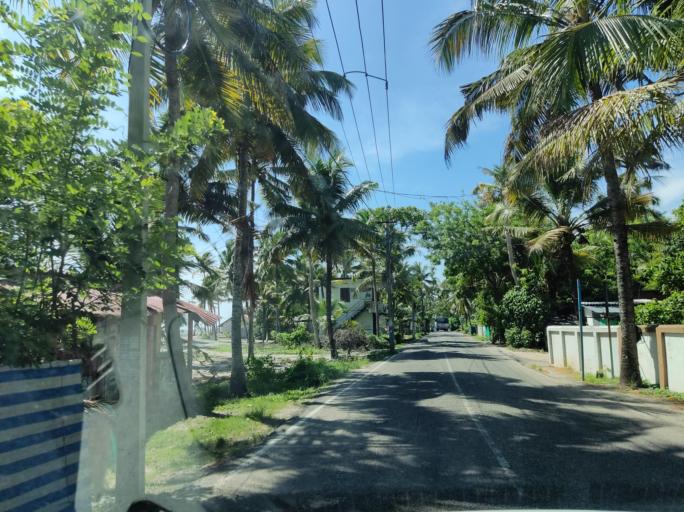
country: IN
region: Kerala
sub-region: Alappuzha
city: Kayankulam
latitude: 9.2383
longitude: 76.4168
